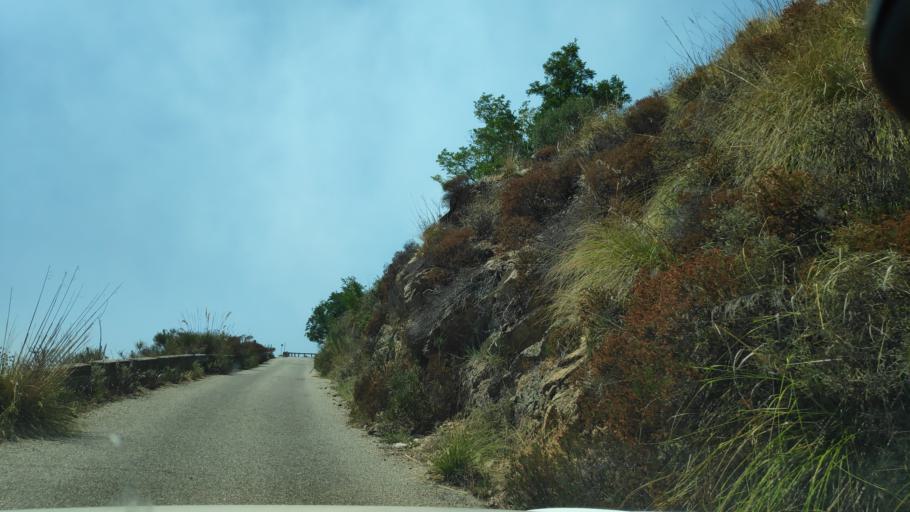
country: IT
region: Calabria
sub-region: Provincia di Reggio Calabria
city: Bova
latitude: 38.0003
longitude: 15.9244
